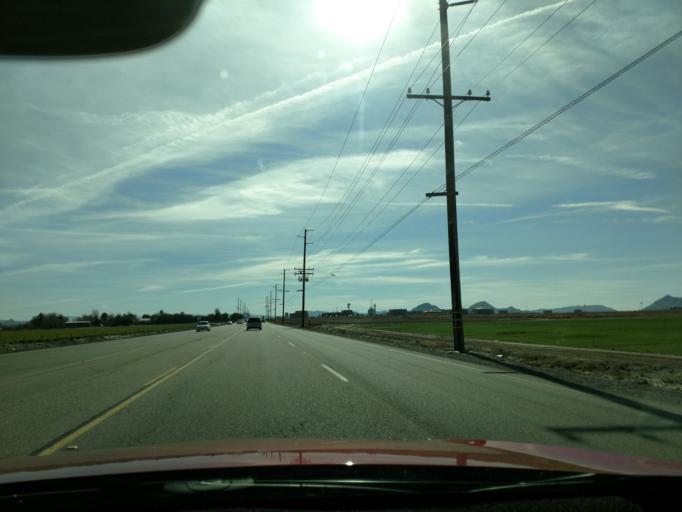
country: US
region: California
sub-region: Riverside County
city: San Jacinto
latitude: 33.8060
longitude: -117.0070
